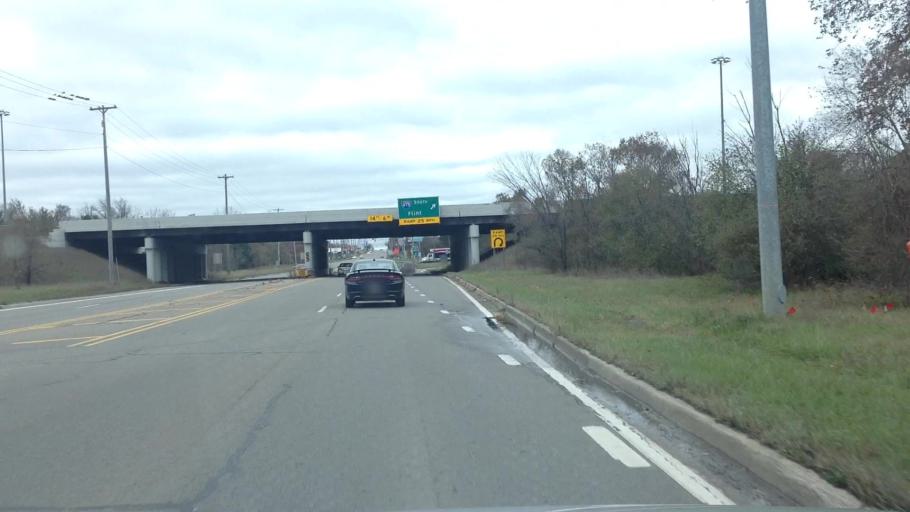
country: US
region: Michigan
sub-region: Genesee County
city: Beecher
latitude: 43.1002
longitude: -83.6943
